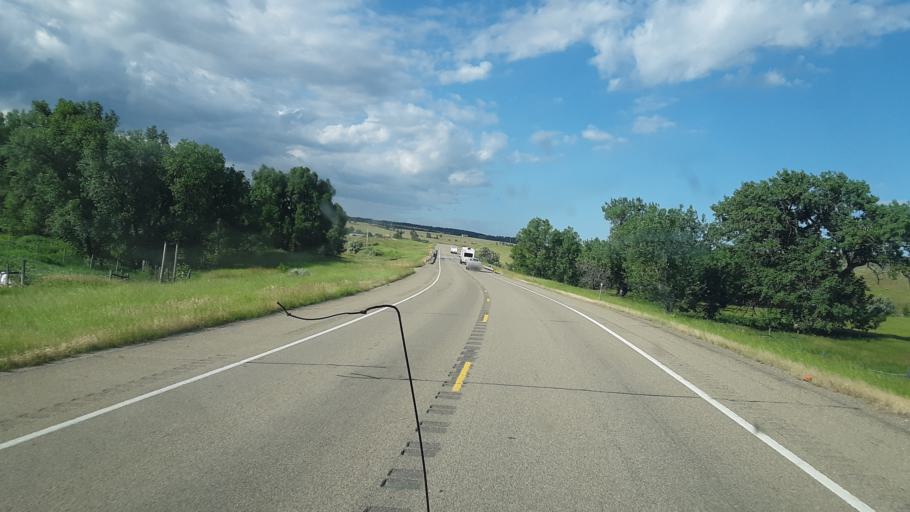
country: US
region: Montana
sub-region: Golden Valley County
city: Ryegate
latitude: 46.3172
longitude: -109.1835
